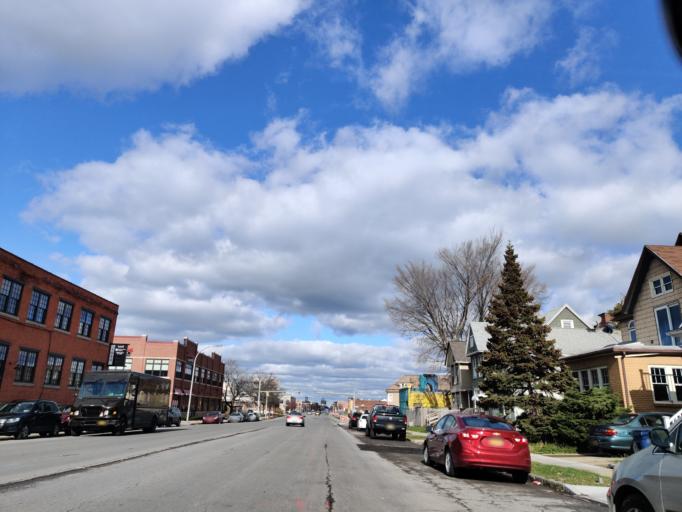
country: US
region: New York
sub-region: Erie County
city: Buffalo
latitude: 42.9118
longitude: -78.8998
